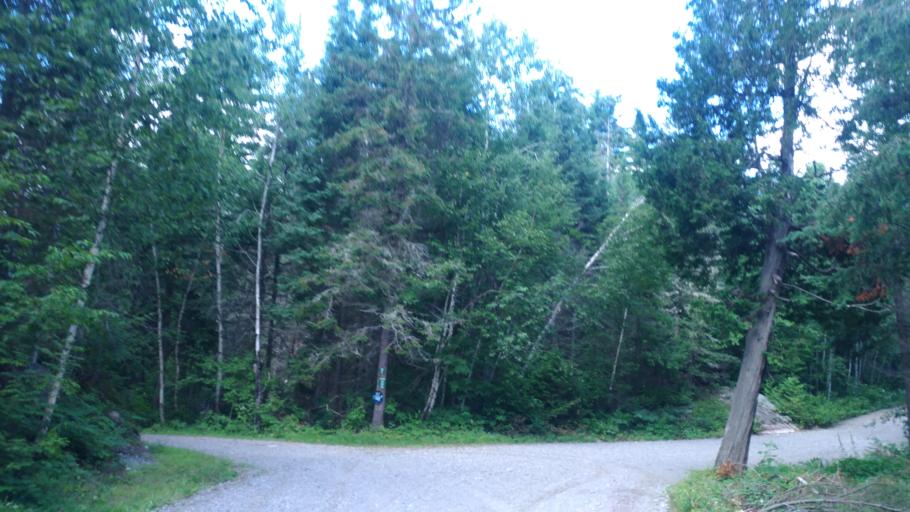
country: CA
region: Ontario
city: Rayside-Balfour
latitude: 46.5906
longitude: -81.5482
